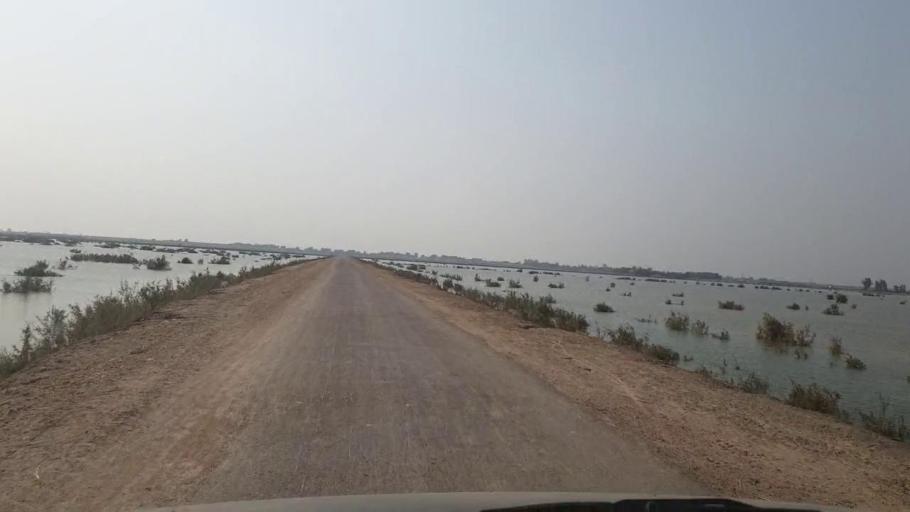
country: PK
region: Sindh
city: Tando Muhammad Khan
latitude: 25.0337
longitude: 68.3930
